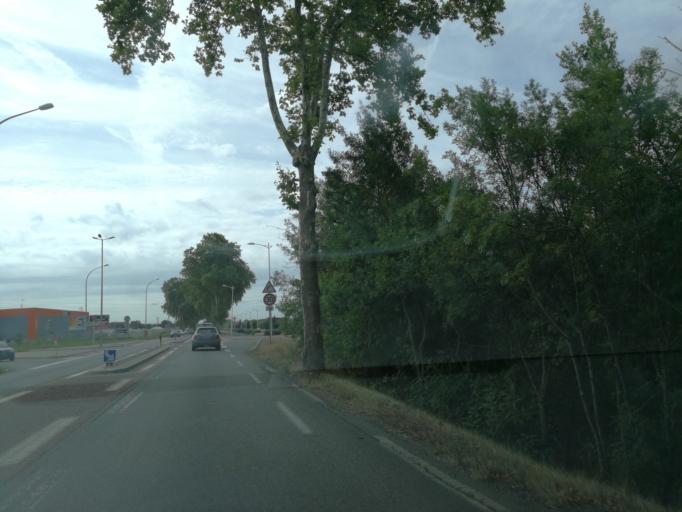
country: FR
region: Midi-Pyrenees
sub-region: Departement de la Haute-Garonne
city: Saint-Alban
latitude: 43.6961
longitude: 1.4000
